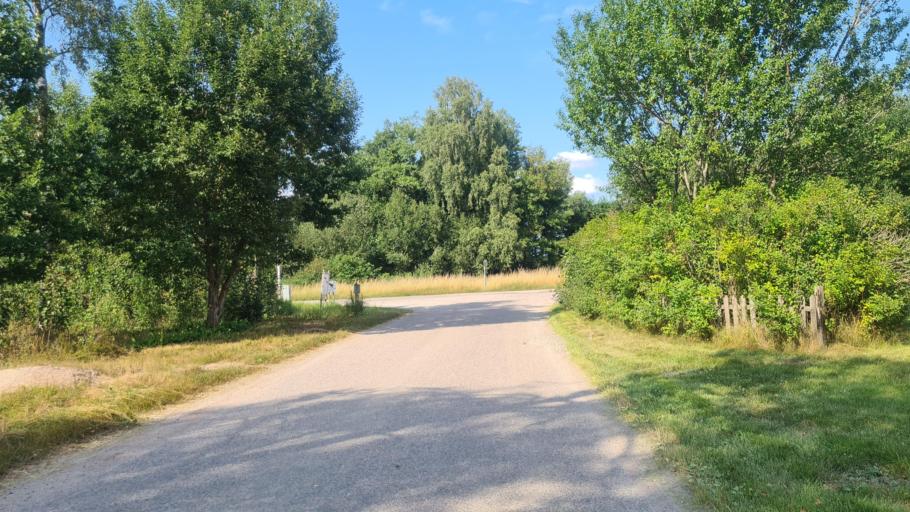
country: SE
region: Kronoberg
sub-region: Ljungby Kommun
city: Ljungby
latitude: 56.7401
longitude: 13.8758
